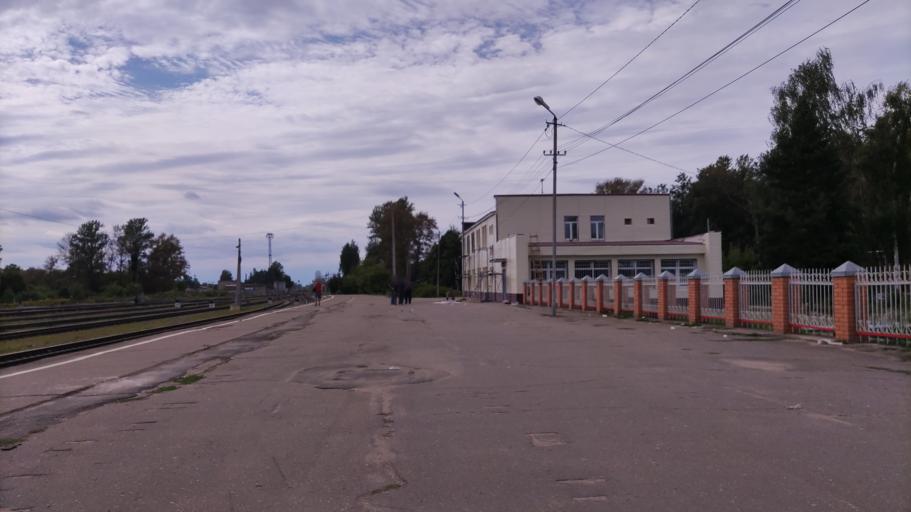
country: RU
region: Tverskaya
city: Rzhev
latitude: 56.2396
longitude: 34.3190
